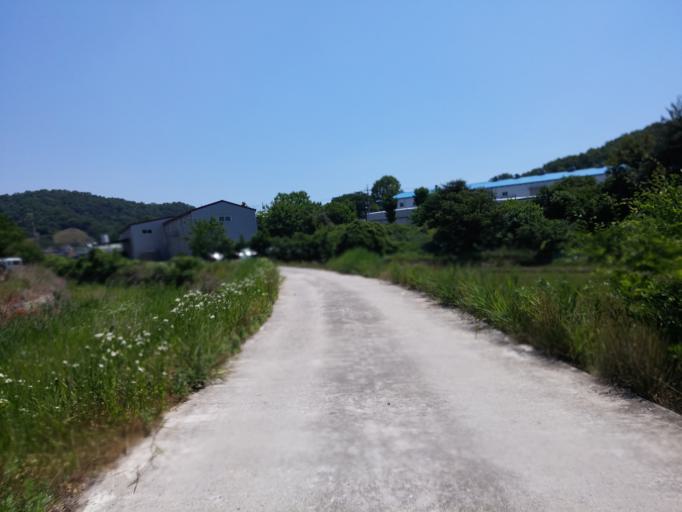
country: KR
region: Chungcheongbuk-do
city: Cheongju-si
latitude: 36.5606
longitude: 127.4376
